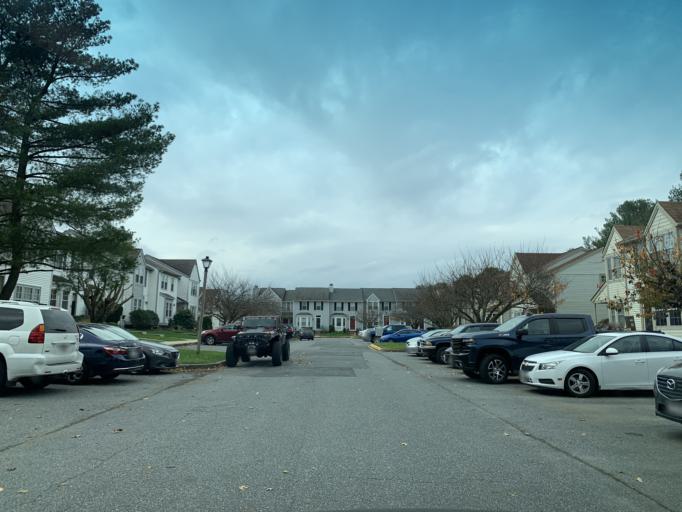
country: US
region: Maryland
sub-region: Harford County
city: Bel Air
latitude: 39.5475
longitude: -76.3451
